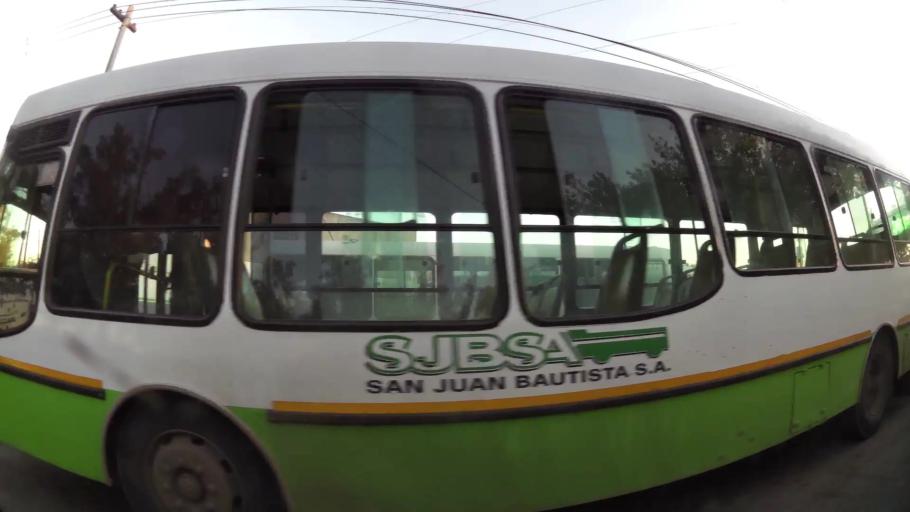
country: AR
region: Buenos Aires
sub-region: Partido de Almirante Brown
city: Adrogue
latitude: -34.8015
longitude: -58.3402
